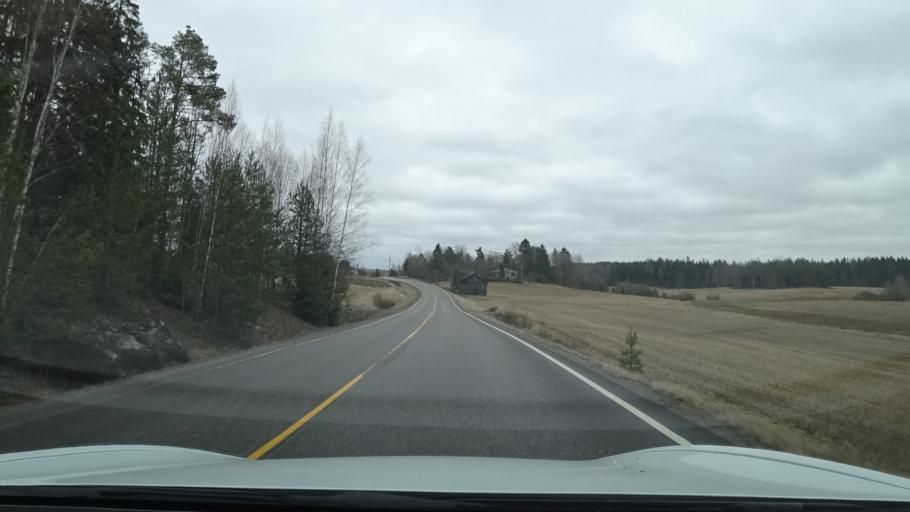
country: FI
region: Uusimaa
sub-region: Porvoo
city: Askola
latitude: 60.4961
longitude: 25.4994
